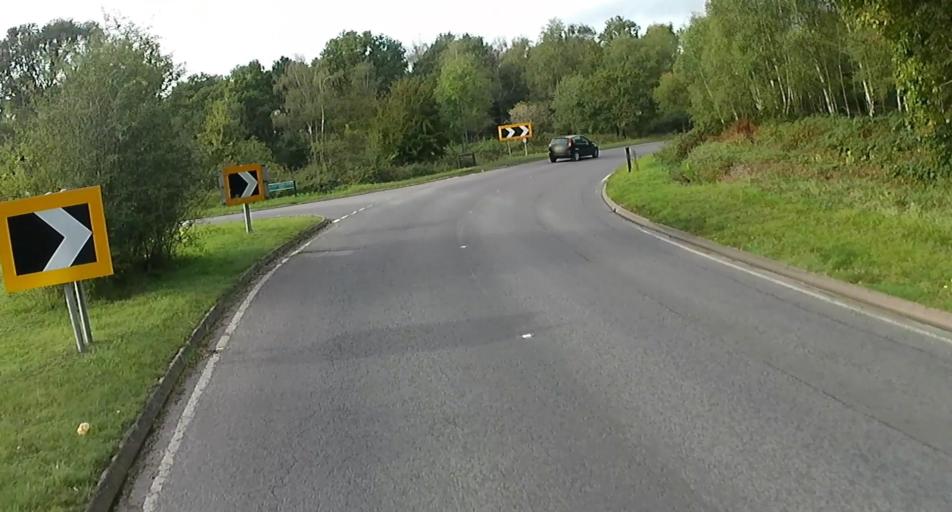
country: GB
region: England
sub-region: West Berkshire
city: Thatcham
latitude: 51.3778
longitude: -1.2482
